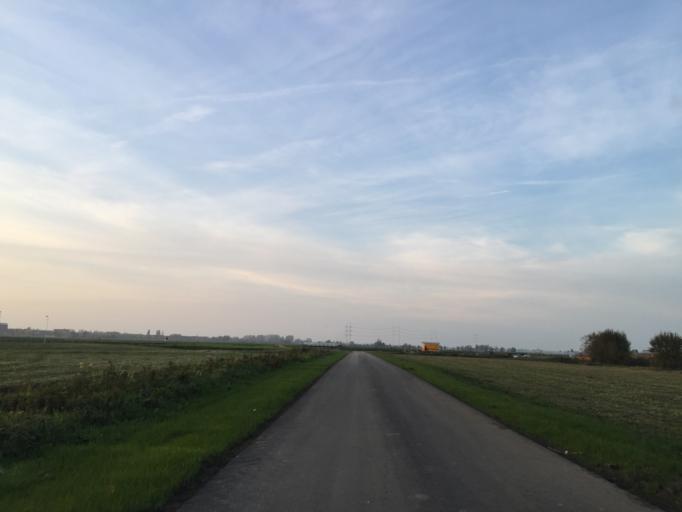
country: NL
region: South Holland
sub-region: Gemeente Lansingerland
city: Berkel en Rodenrijs
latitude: 52.0020
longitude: 4.4661
